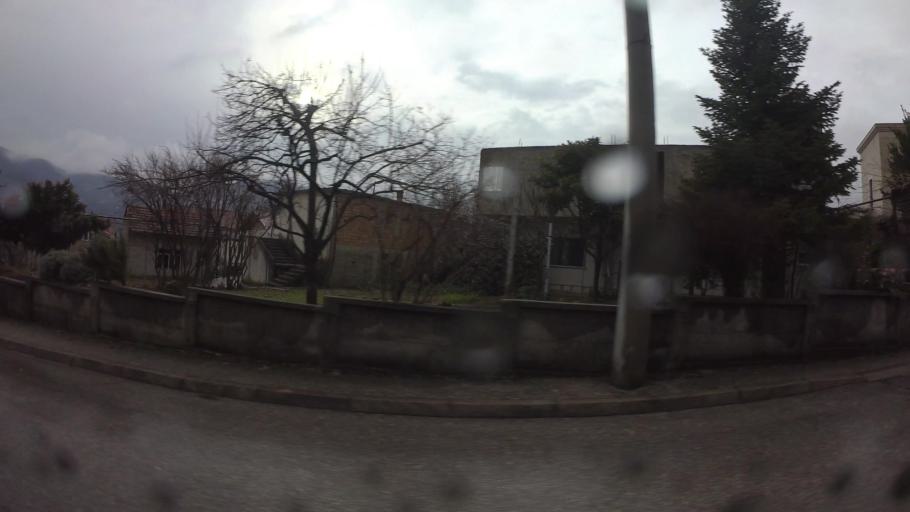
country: BA
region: Federation of Bosnia and Herzegovina
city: Cim
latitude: 43.3540
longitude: 17.7761
